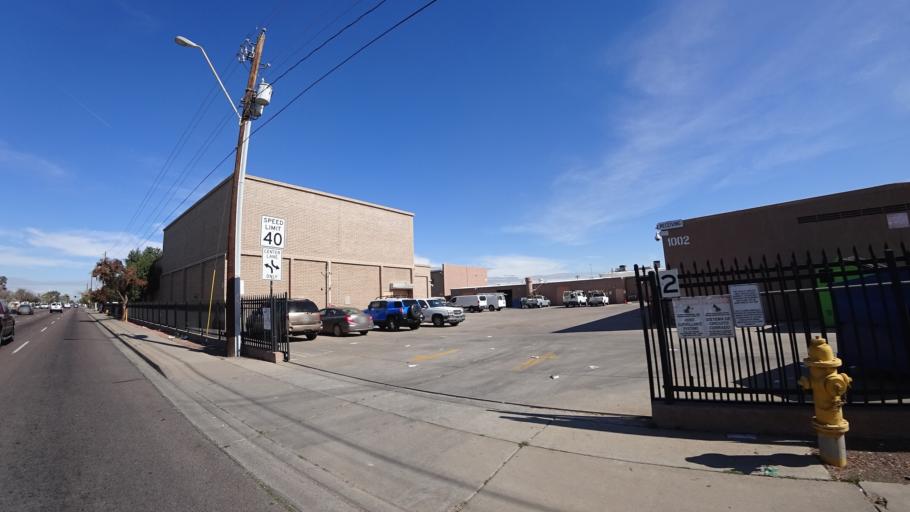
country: US
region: Arizona
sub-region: Maricopa County
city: Glendale
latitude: 33.4884
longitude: -112.2032
